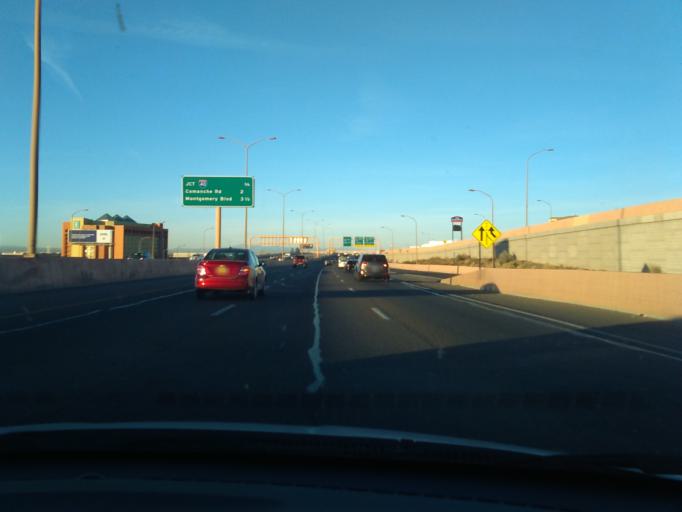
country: US
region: New Mexico
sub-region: Bernalillo County
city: Albuquerque
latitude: 35.0875
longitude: -106.6356
